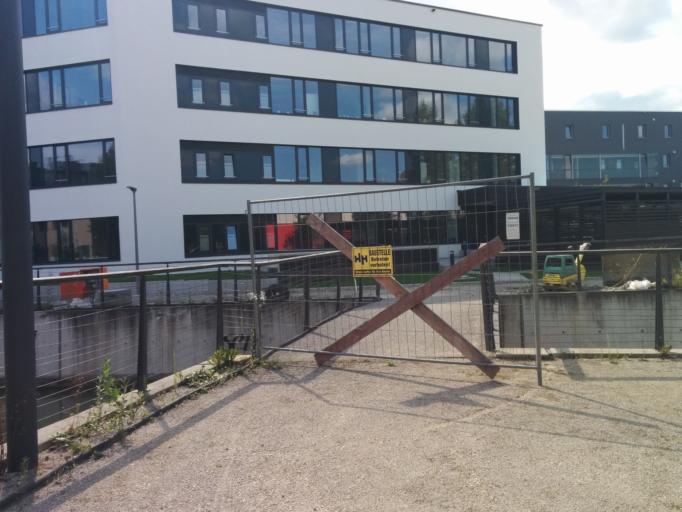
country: DE
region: Bavaria
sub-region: Upper Bavaria
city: Rosenheim
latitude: 47.8572
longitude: 12.1334
